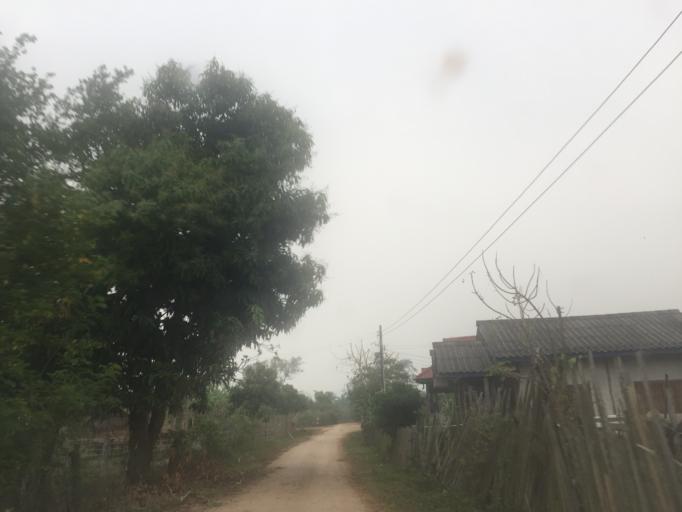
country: LA
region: Xiagnabouli
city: Sainyabuli
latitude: 19.0455
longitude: 101.5133
